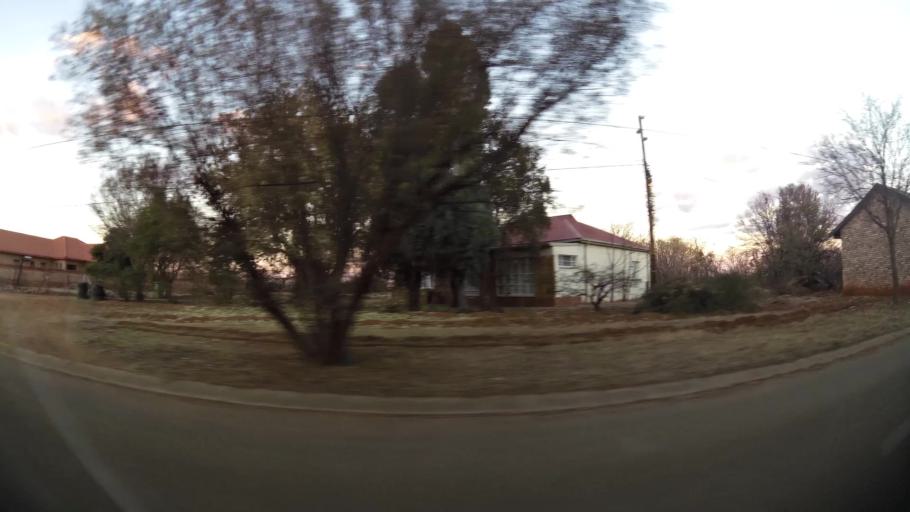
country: ZA
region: North-West
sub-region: Dr Kenneth Kaunda District Municipality
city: Potchefstroom
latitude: -26.7156
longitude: 27.1235
